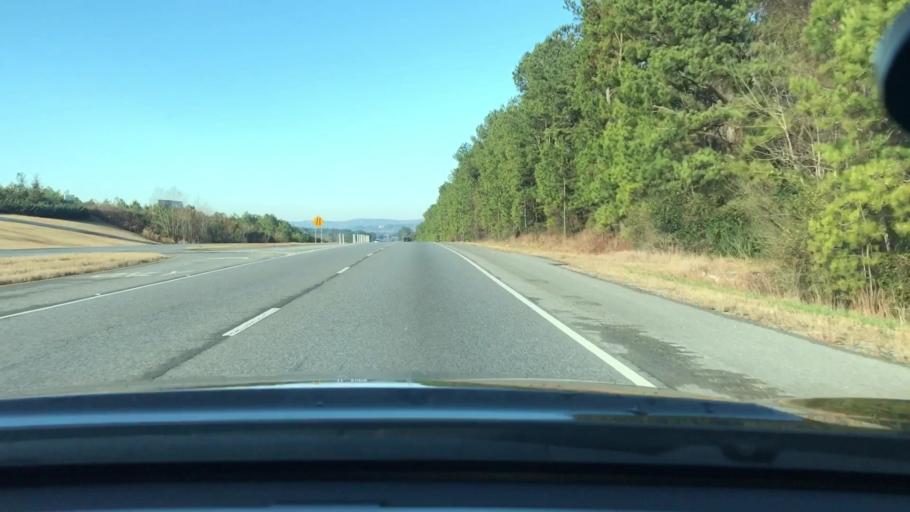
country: US
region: Alabama
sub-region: Shelby County
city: Chelsea
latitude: 33.3503
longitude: -86.5848
